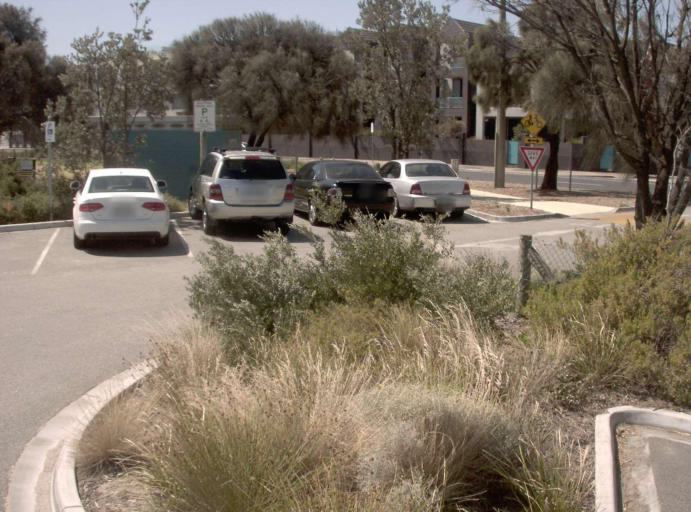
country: AU
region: Victoria
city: Hampton
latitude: -37.9531
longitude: 145.0041
